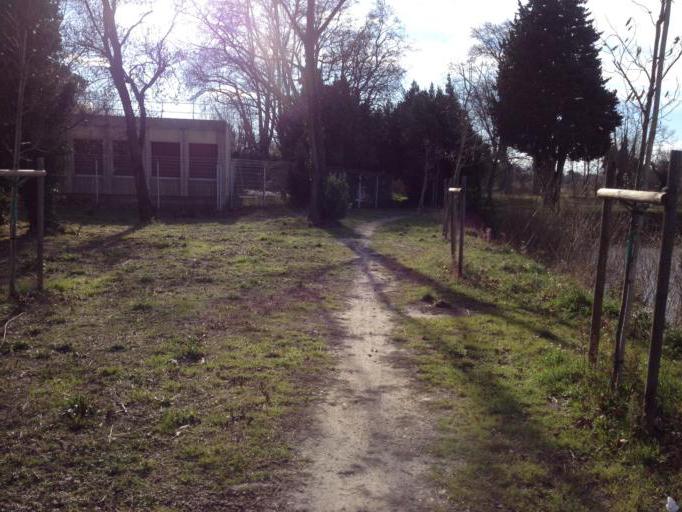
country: FR
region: Provence-Alpes-Cote d'Azur
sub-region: Departement du Vaucluse
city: Orange
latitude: 44.1342
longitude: 4.7970
